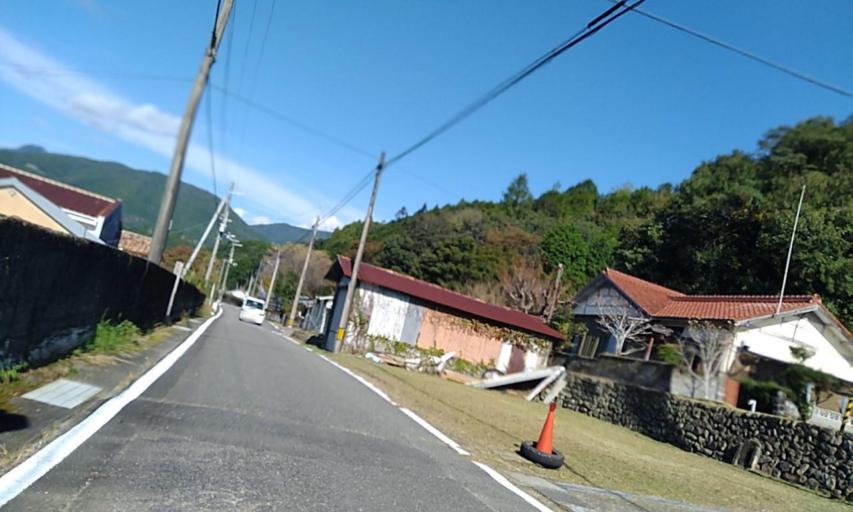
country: JP
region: Wakayama
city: Shingu
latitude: 33.9244
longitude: 135.9839
